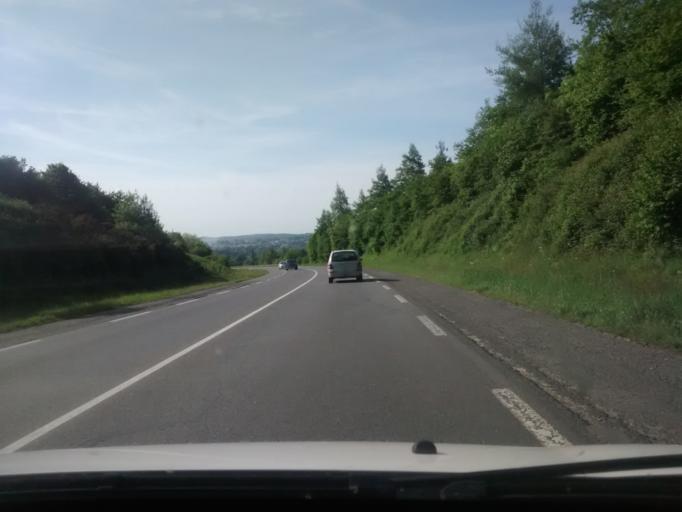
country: FR
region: Brittany
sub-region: Departement d'Ille-et-Vilaine
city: Lecousse
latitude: 48.3490
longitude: -1.2289
